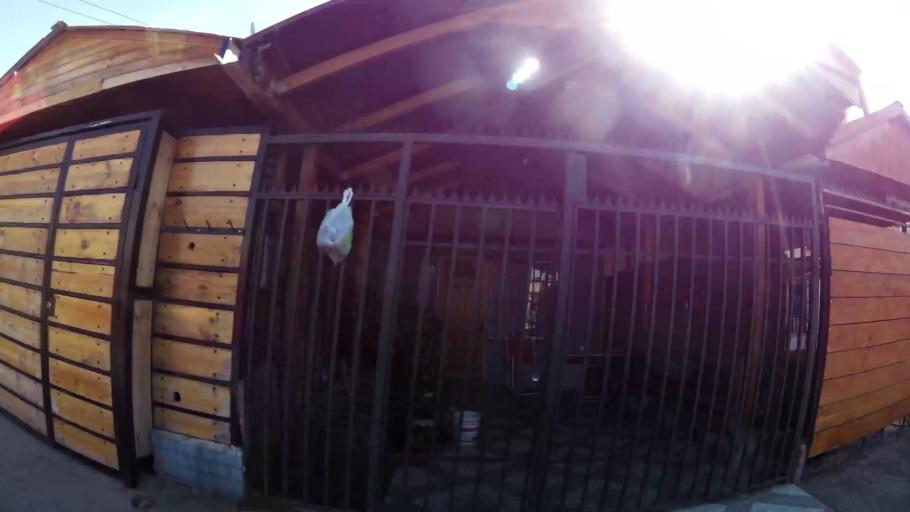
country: CL
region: Santiago Metropolitan
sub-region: Provincia de Santiago
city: La Pintana
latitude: -33.5646
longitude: -70.6218
